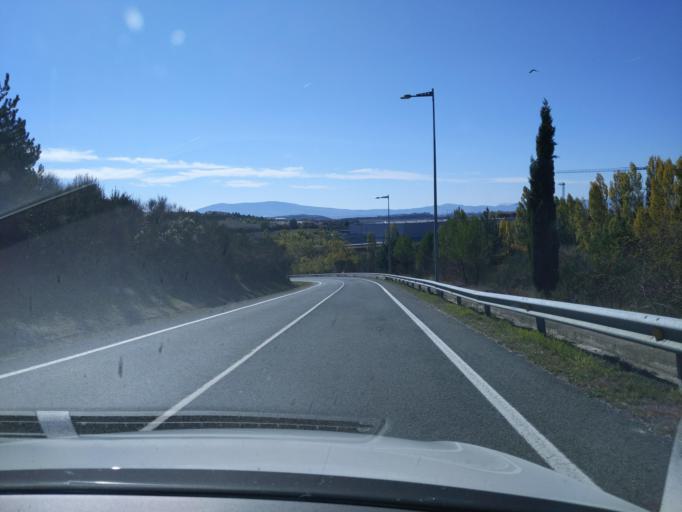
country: ES
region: Navarre
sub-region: Provincia de Navarra
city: Egues-Uharte
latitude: 42.8333
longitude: -1.5705
